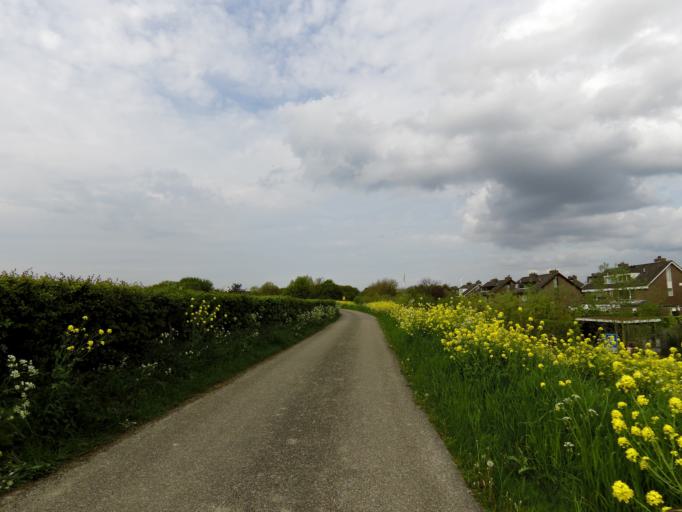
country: NL
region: South Holland
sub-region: Gemeente Brielle
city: Brielle
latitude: 51.9110
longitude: 4.1662
